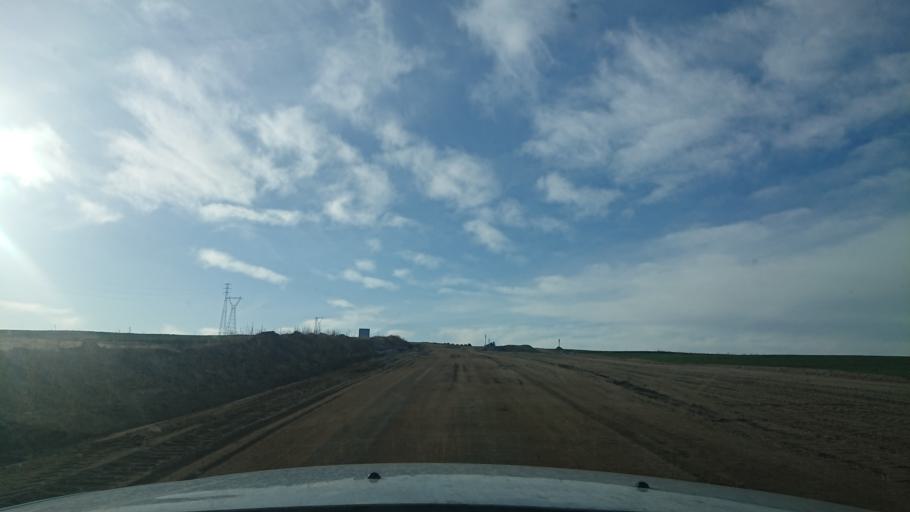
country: TR
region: Aksaray
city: Agacoren
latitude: 38.8519
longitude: 33.9428
